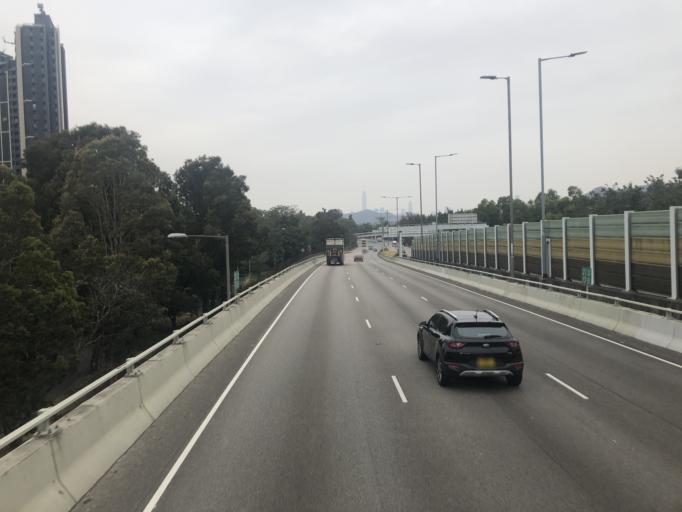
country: HK
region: Tai Po
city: Tai Po
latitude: 22.5002
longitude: 114.1233
